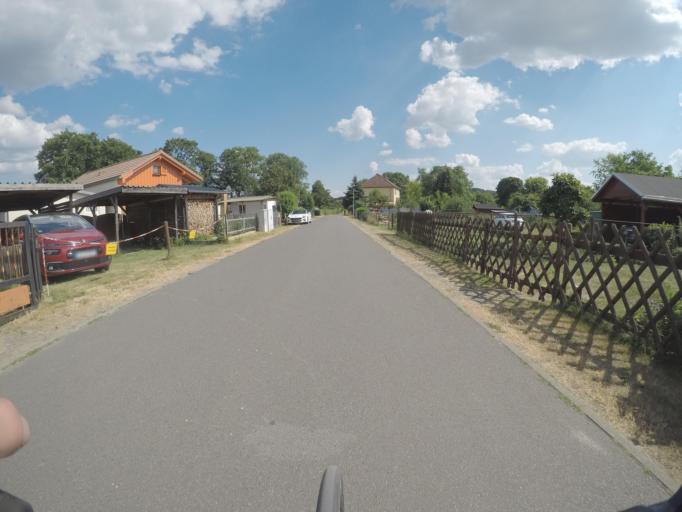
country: DE
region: Brandenburg
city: Ketzin
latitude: 52.4306
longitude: 12.8819
